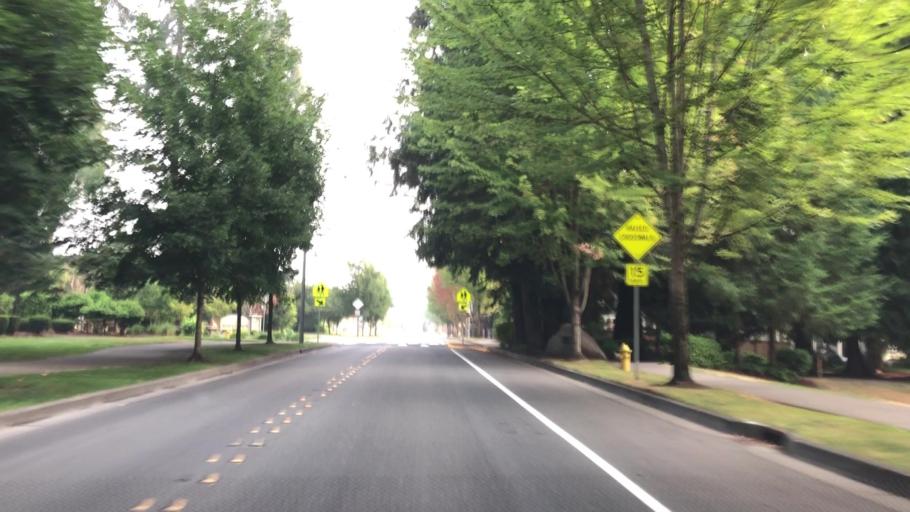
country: US
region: Washington
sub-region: King County
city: Redmond
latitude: 47.7063
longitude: -122.1108
